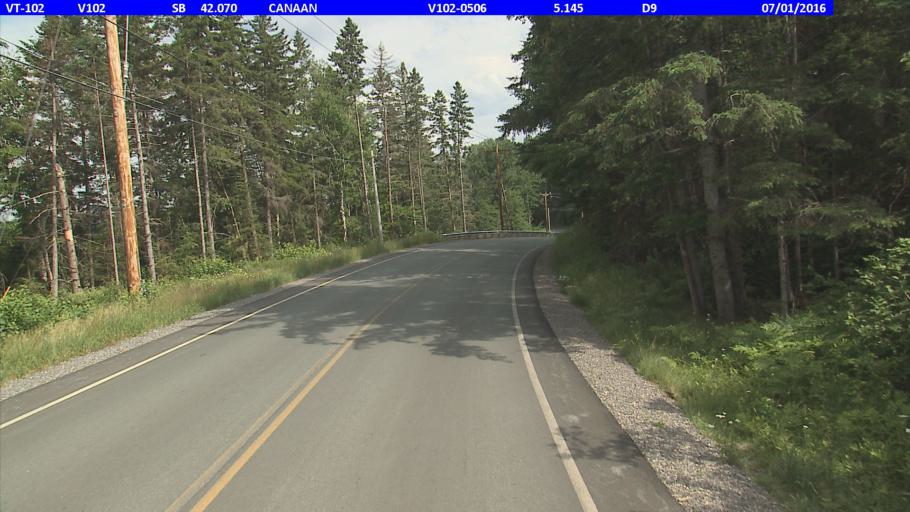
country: US
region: New Hampshire
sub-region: Coos County
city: Colebrook
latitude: 44.9748
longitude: -71.5360
